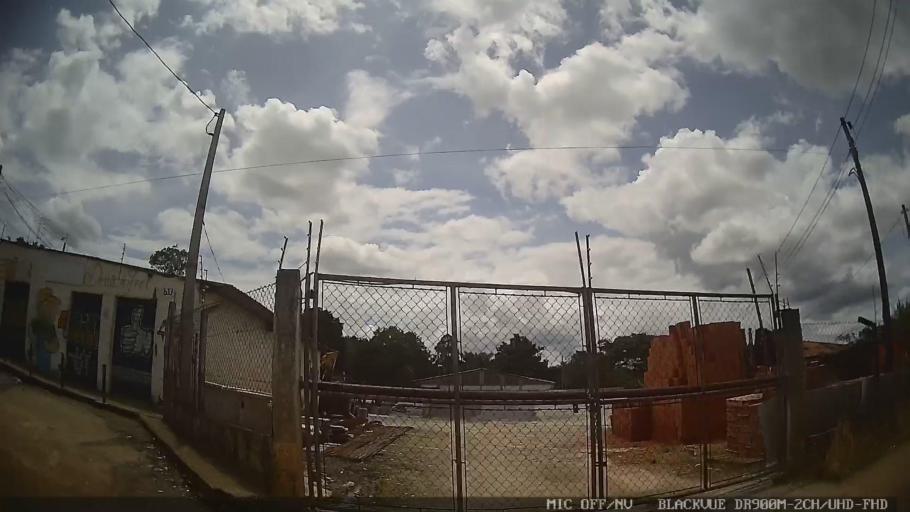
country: BR
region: Sao Paulo
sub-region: Mogi das Cruzes
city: Mogi das Cruzes
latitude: -23.5908
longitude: -46.2335
